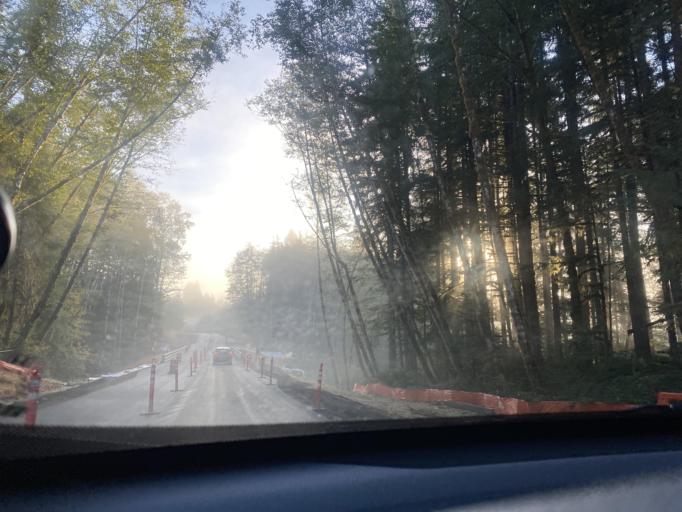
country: US
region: Washington
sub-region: Clallam County
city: Forks
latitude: 47.8133
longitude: -124.0720
